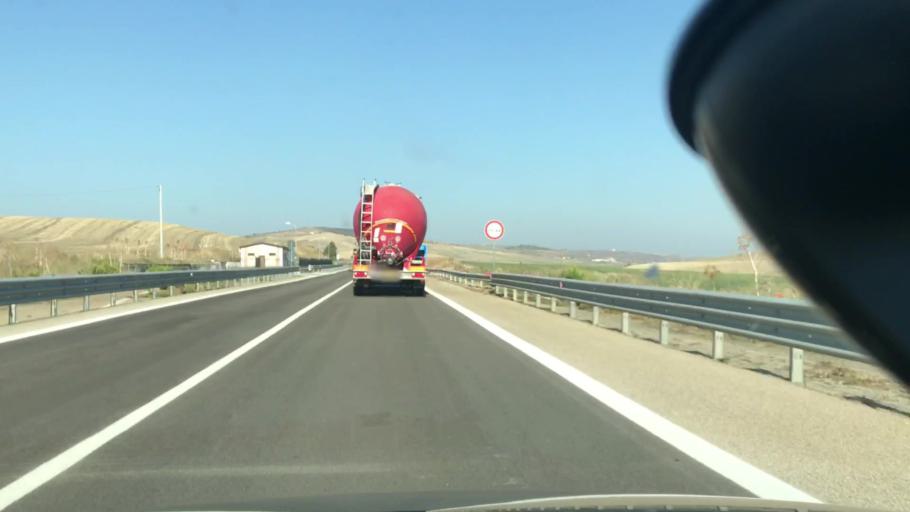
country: IT
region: Basilicate
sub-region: Provincia di Matera
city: Irsina
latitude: 40.7855
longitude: 16.2977
